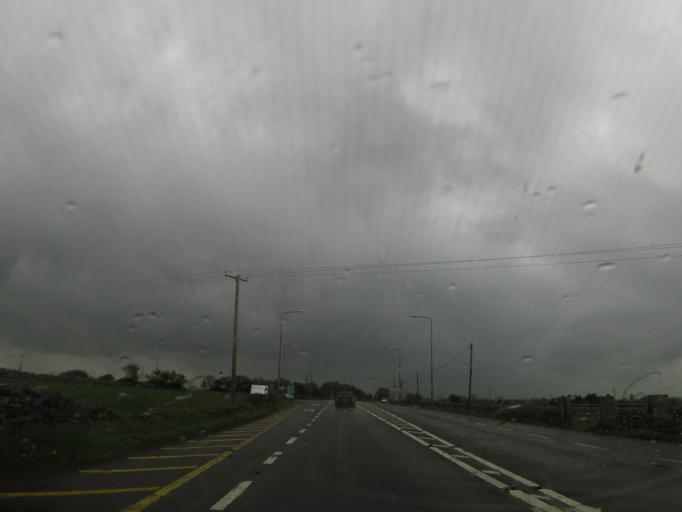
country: IE
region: Connaught
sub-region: County Galway
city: Claregalway
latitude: 53.3630
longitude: -8.9259
